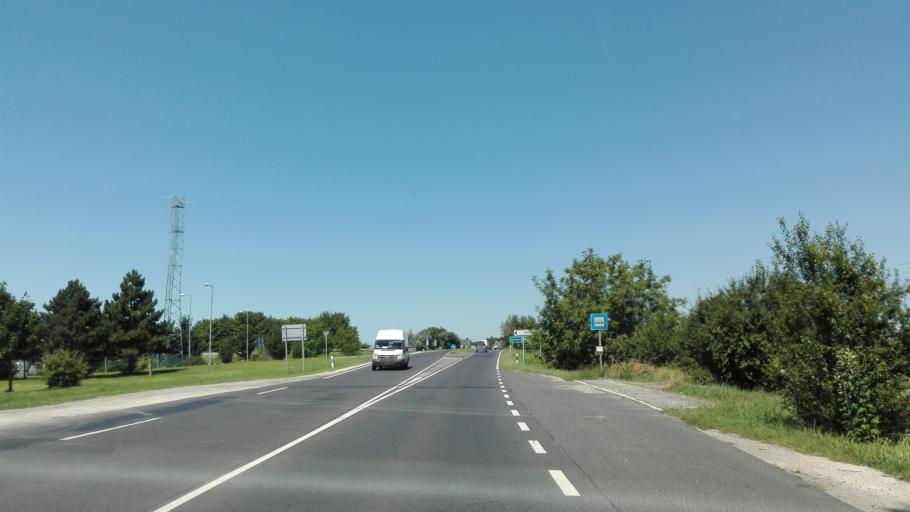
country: HU
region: Fejer
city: Lepseny
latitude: 46.9886
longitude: 18.1903
